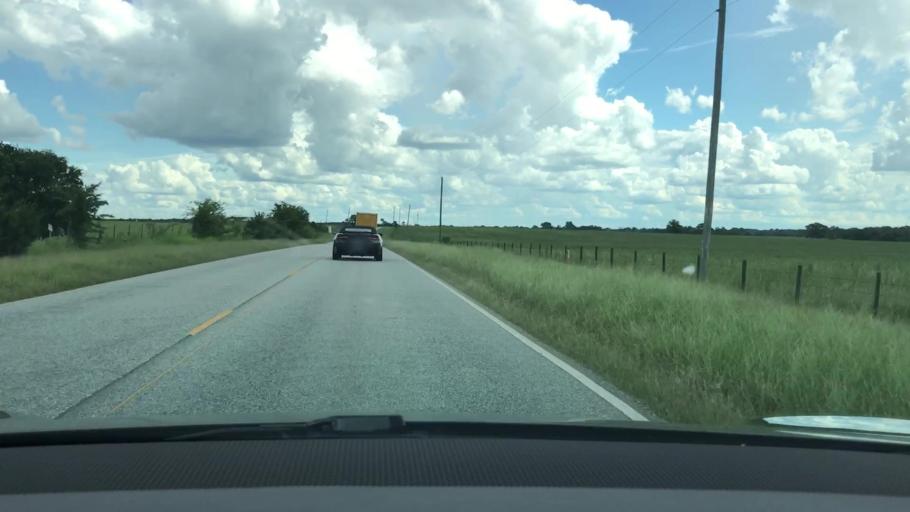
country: US
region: Alabama
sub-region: Montgomery County
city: Pike Road
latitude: 32.2768
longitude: -86.1012
